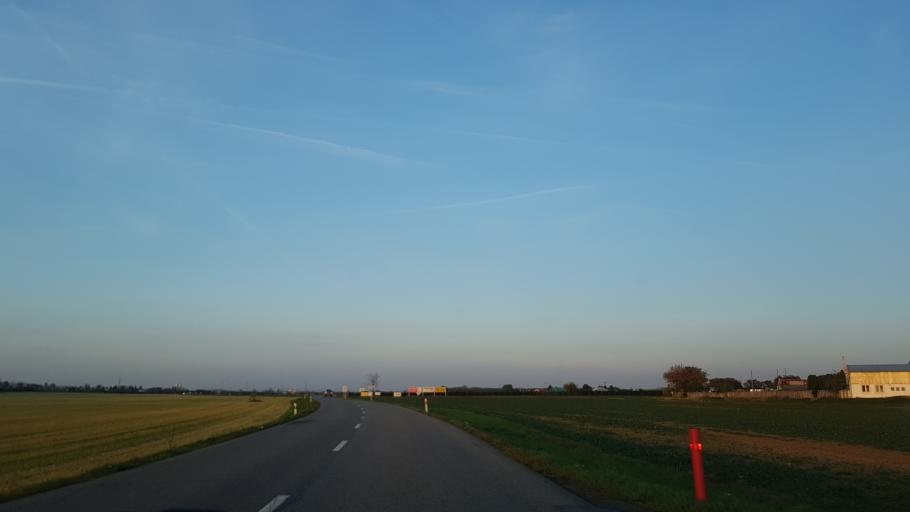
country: CZ
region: Zlin
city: Nedakonice
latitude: 49.0430
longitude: 17.3925
